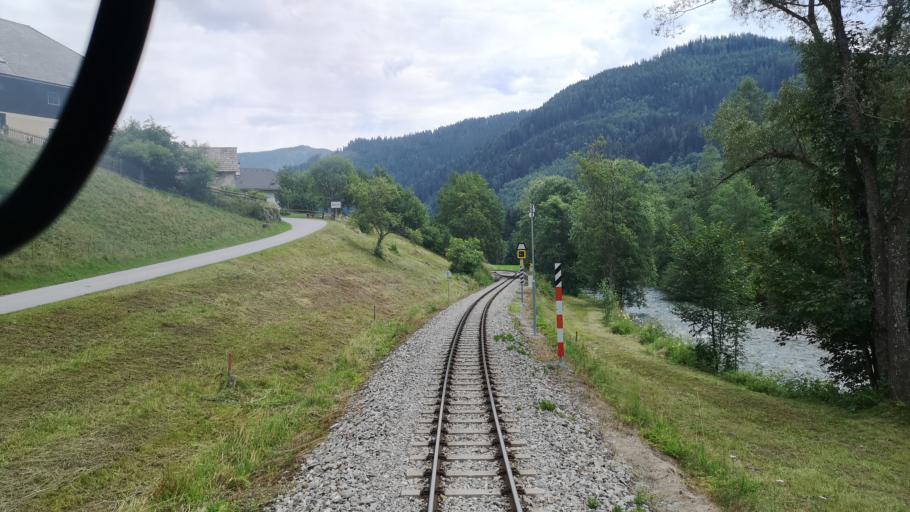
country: AT
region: Salzburg
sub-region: Politischer Bezirk Tamsweg
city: Ramingstein
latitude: 47.0708
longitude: 13.8775
